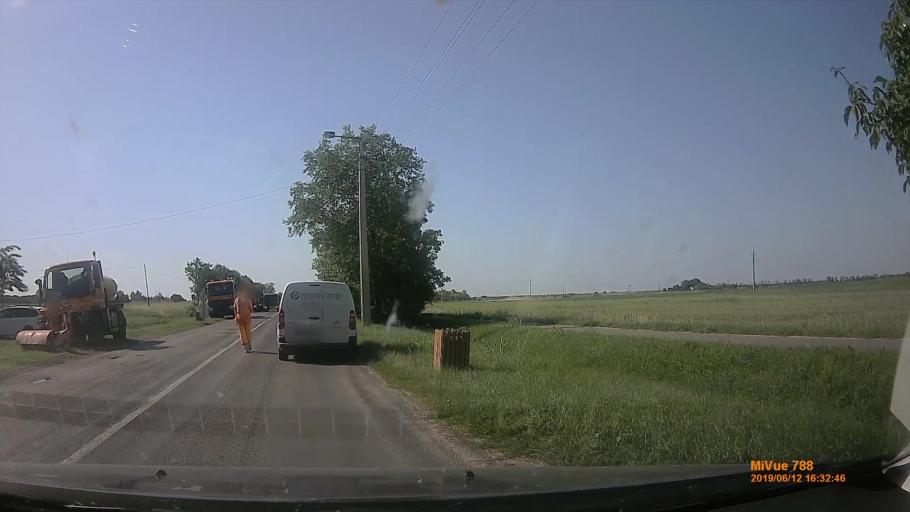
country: HU
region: Csongrad
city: Apatfalva
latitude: 46.1827
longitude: 20.5697
